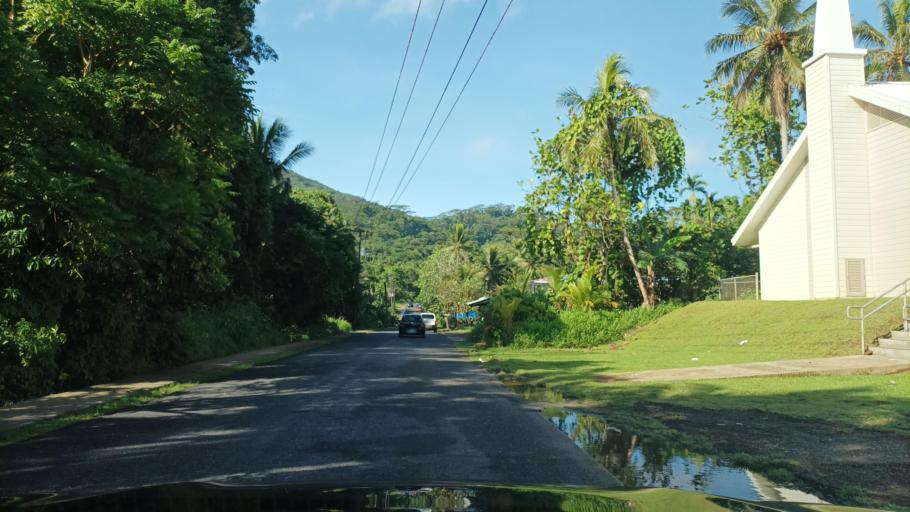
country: FM
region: Pohnpei
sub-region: Sokehs Municipality
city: Palikir - National Government Center
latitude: 6.9334
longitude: 158.1809
